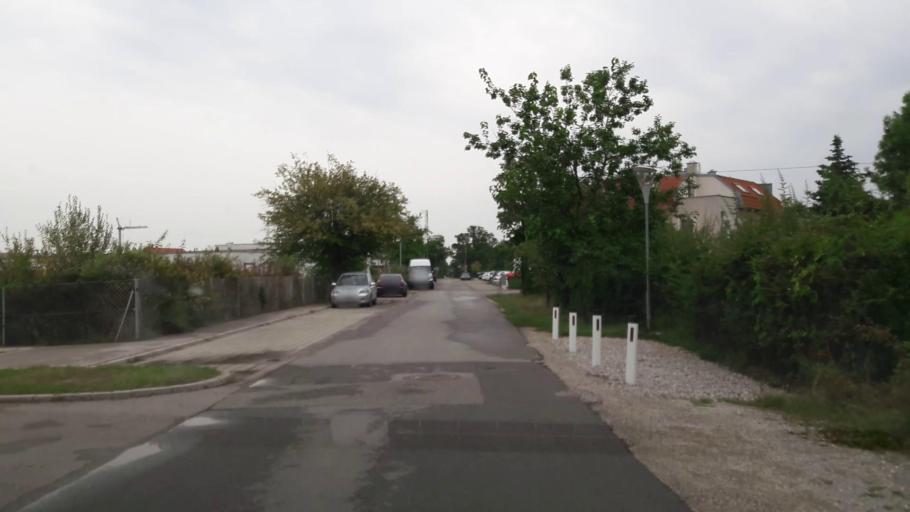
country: AT
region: Lower Austria
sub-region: Politischer Bezirk Ganserndorf
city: Strasshof an der Nordbahn
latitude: 48.3238
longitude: 16.6440
